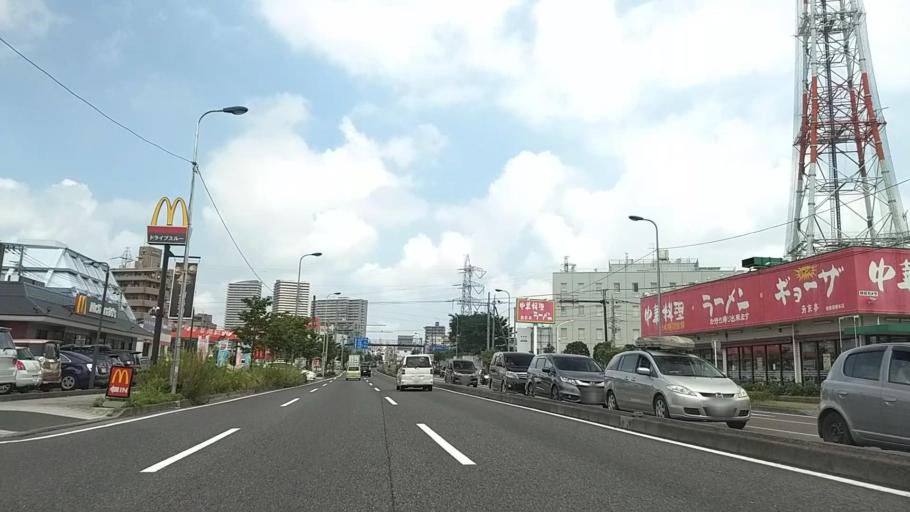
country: JP
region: Tokyo
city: Hachioji
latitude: 35.5897
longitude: 139.3422
